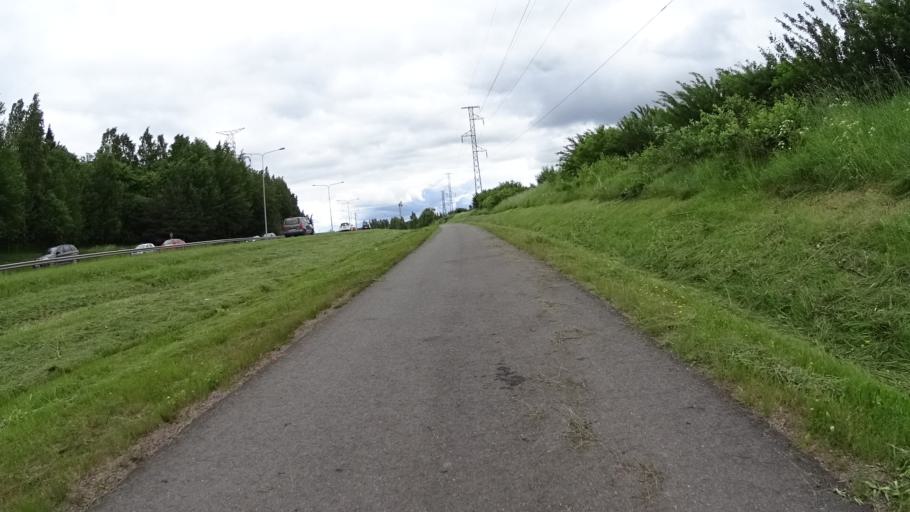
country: FI
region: Uusimaa
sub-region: Helsinki
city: Kilo
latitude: 60.2730
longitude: 24.7968
